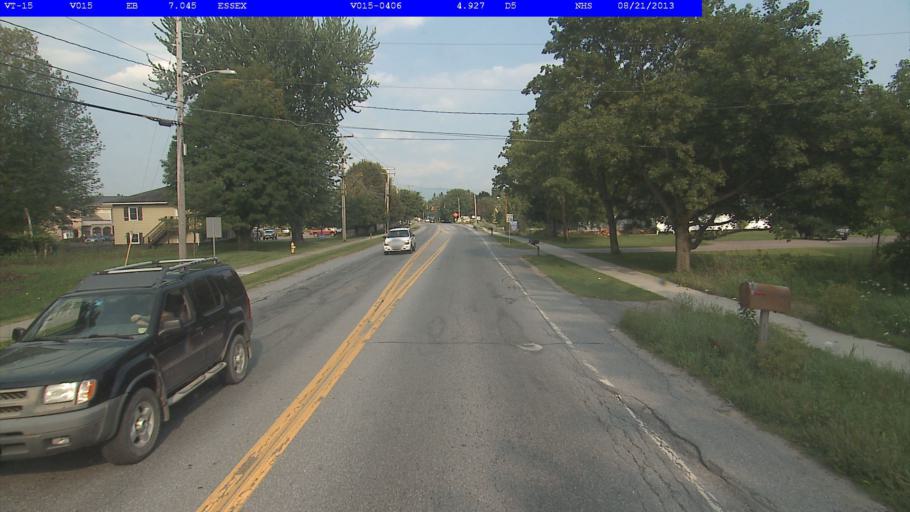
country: US
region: Vermont
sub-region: Chittenden County
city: Essex Junction
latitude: 44.5107
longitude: -73.0680
